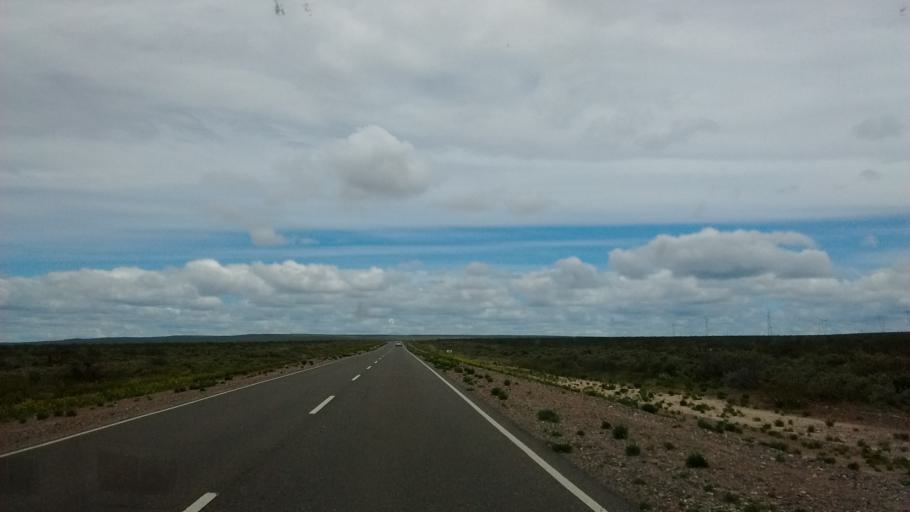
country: AR
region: Neuquen
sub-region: Departamento de Picun Leufu
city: Picun Leufu
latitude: -39.7040
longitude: -69.5005
